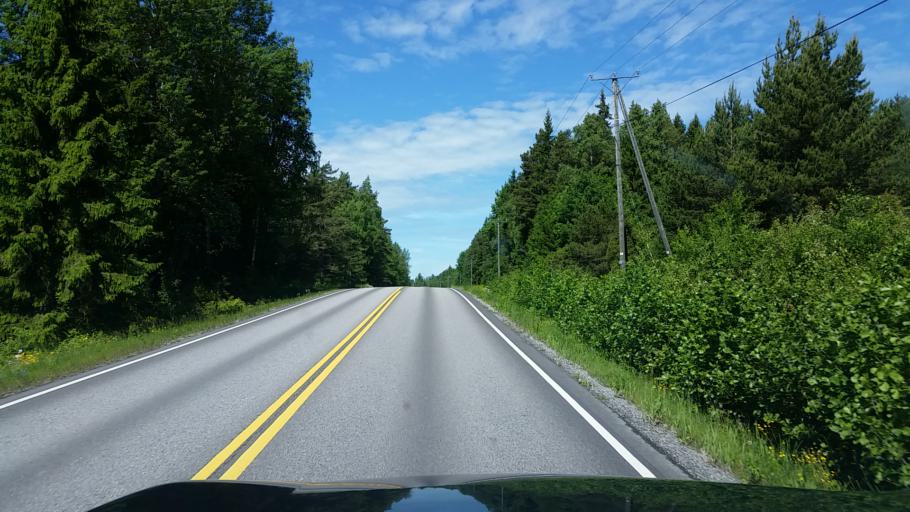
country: FI
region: Varsinais-Suomi
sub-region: Aboland-Turunmaa
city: Laensi-Turunmaa
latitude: 60.2415
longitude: 22.1525
